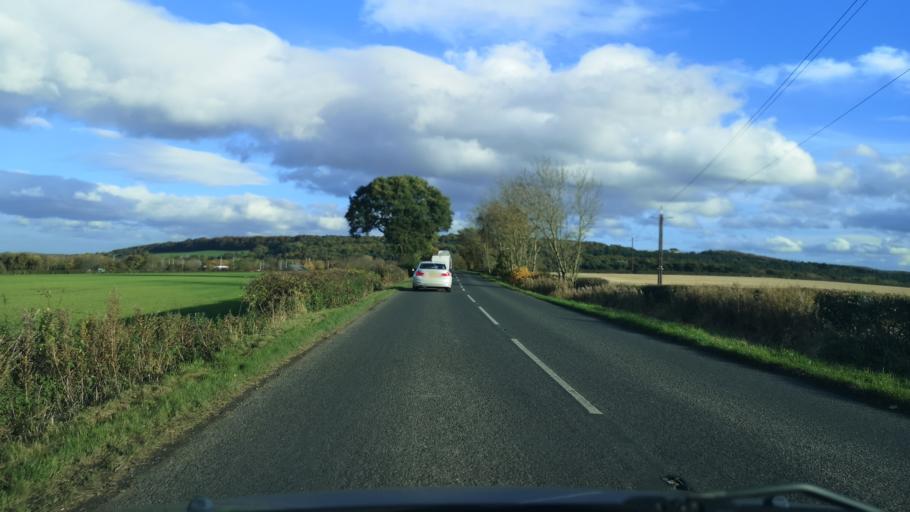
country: GB
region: England
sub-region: City and Borough of Wakefield
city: Crigglestone
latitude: 53.6216
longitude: -1.5573
